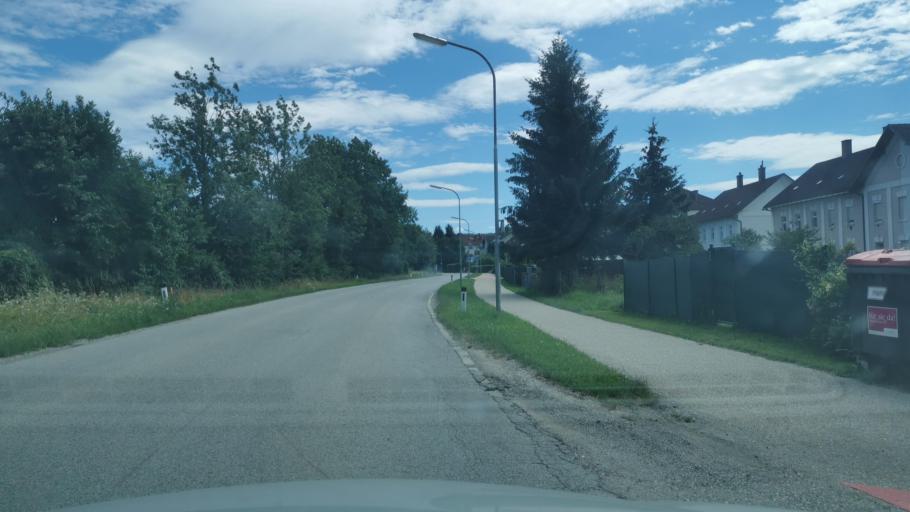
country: AT
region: Lower Austria
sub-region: Sankt Polten Stadt
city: Sankt Poelten
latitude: 48.1638
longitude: 15.6377
